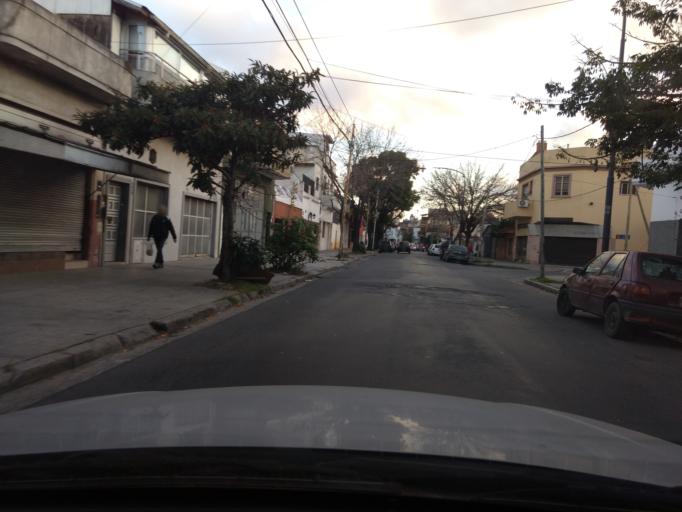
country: AR
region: Buenos Aires F.D.
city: Villa Santa Rita
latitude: -34.6160
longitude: -58.5118
